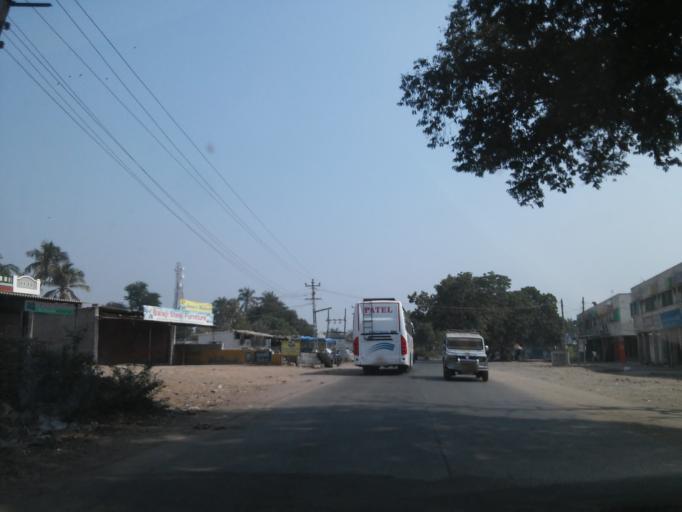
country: IN
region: Gujarat
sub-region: Kachchh
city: Mundra
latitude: 22.8399
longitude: 69.7130
